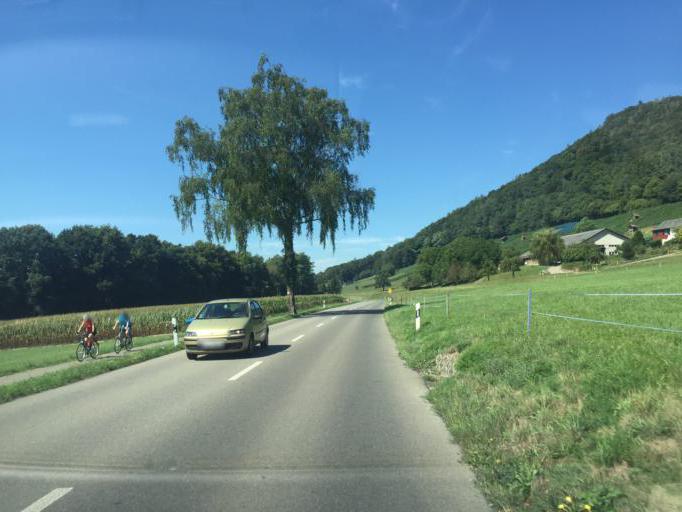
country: CH
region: Thurgau
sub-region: Frauenfeld District
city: Wagenhausen
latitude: 47.6683
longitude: 8.8442
